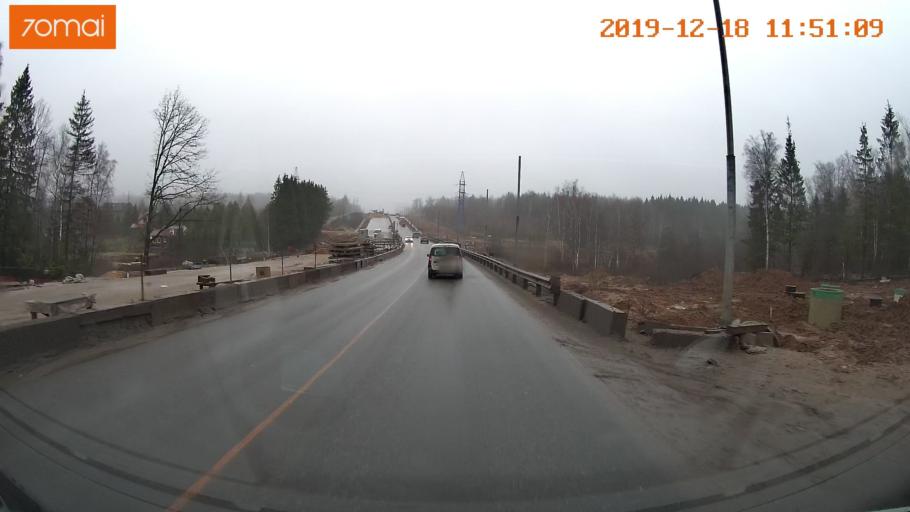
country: RU
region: Moskovskaya
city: Yershovo
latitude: 55.7914
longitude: 36.9218
